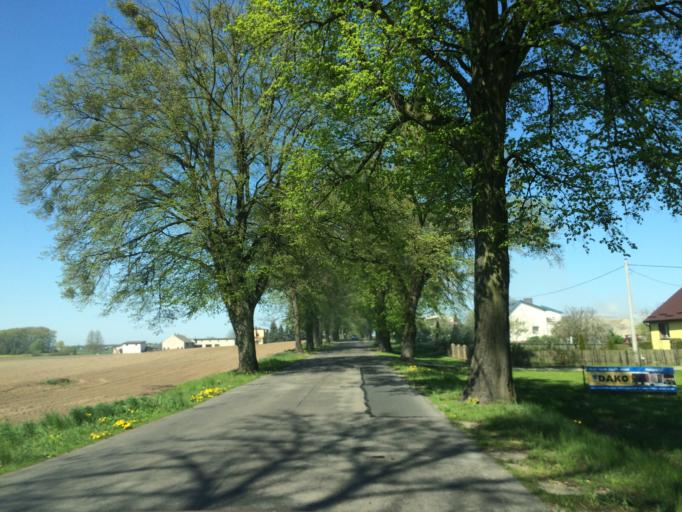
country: PL
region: Warmian-Masurian Voivodeship
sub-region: Powiat nowomiejski
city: Biskupiec
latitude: 53.4964
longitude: 19.3791
